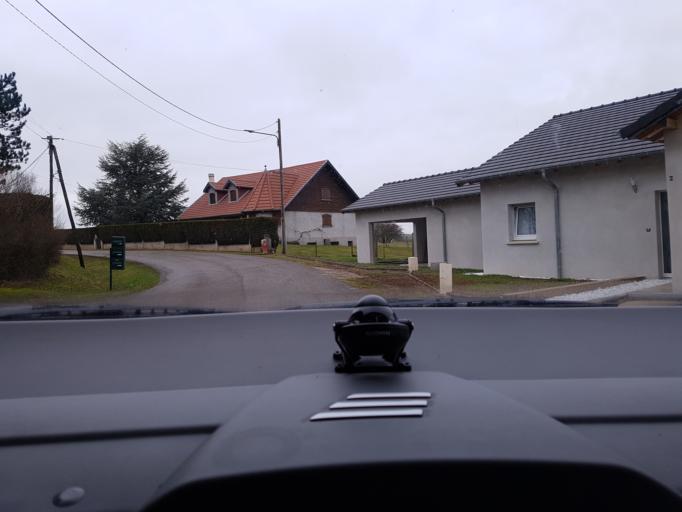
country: FR
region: Lorraine
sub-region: Departement de la Moselle
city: Morhange
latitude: 48.9597
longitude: 6.6521
